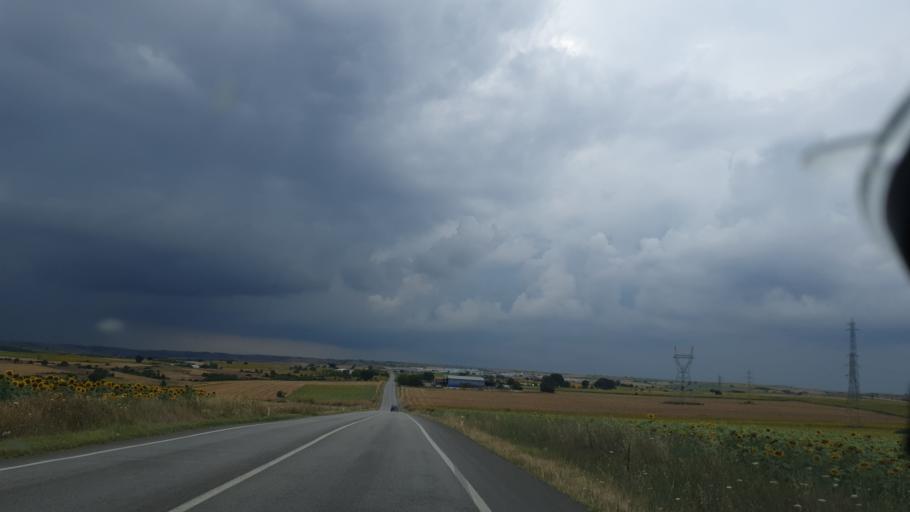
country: TR
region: Tekirdag
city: Hayrabolu
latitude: 41.2182
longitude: 27.0851
